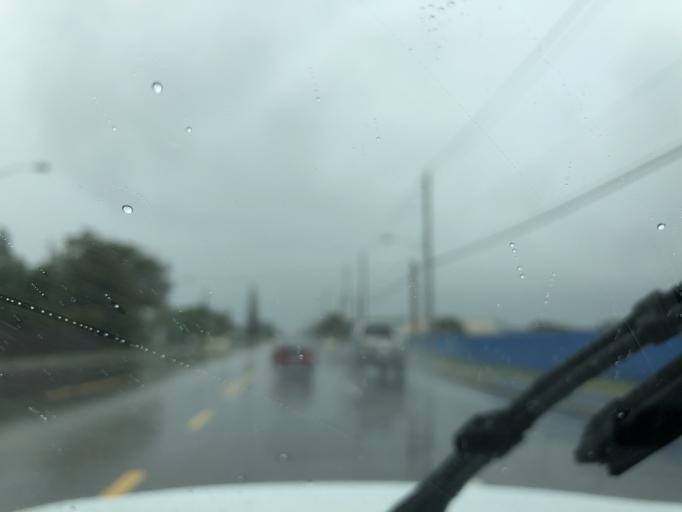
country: US
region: Florida
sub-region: Palm Beach County
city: Royal Palm Estates
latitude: 26.6835
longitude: -80.1201
